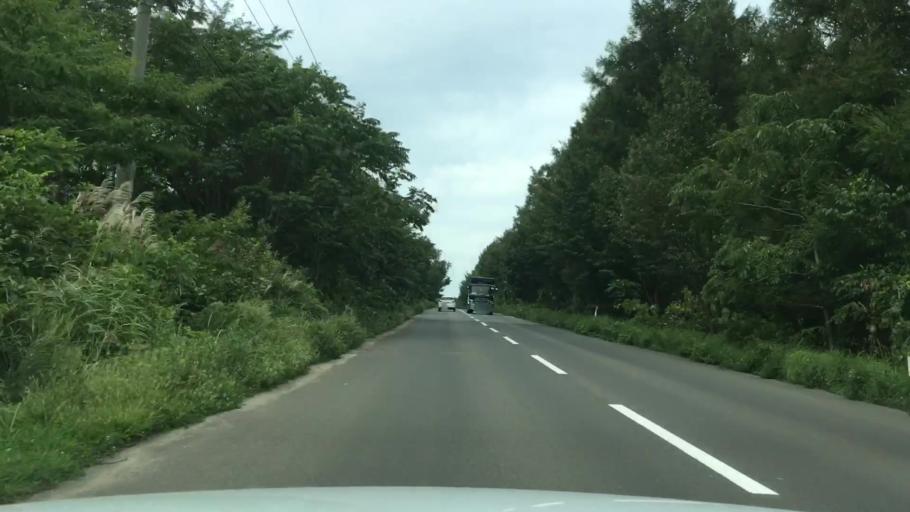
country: JP
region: Aomori
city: Shimokizukuri
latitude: 40.7117
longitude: 140.3290
